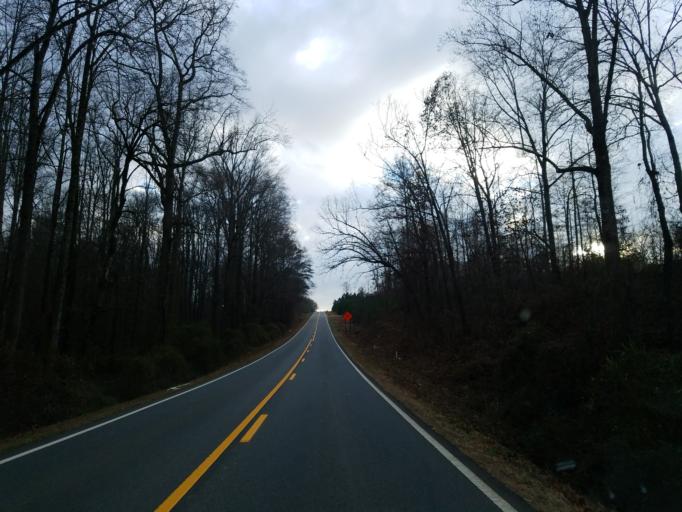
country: US
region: Georgia
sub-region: Dawson County
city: Dawsonville
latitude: 34.3291
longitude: -84.0698
